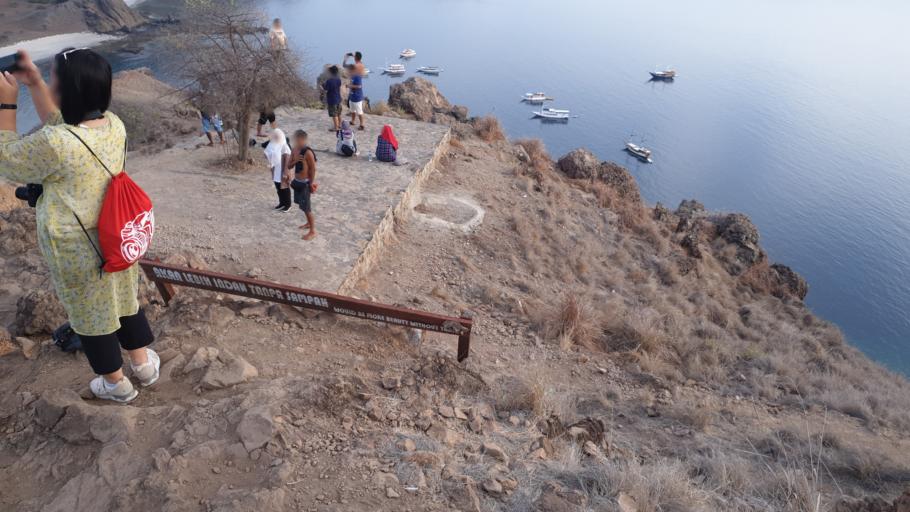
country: ID
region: East Nusa Tenggara
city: Komodo
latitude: -8.6809
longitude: 119.5568
